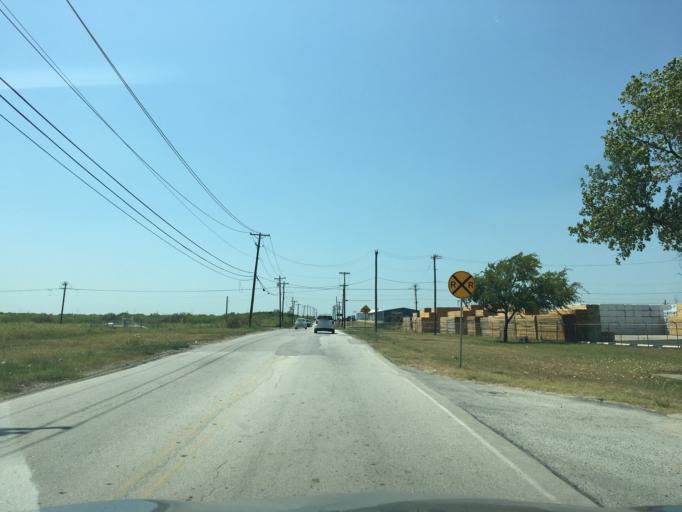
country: US
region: Texas
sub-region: Tarrant County
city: Everman
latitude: 32.6140
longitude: -97.3292
